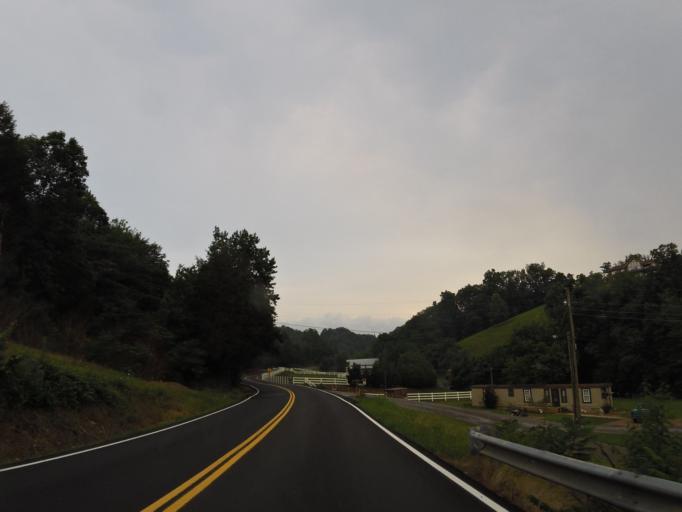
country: US
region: Tennessee
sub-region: Sevier County
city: Sevierville
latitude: 35.8373
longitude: -83.6362
